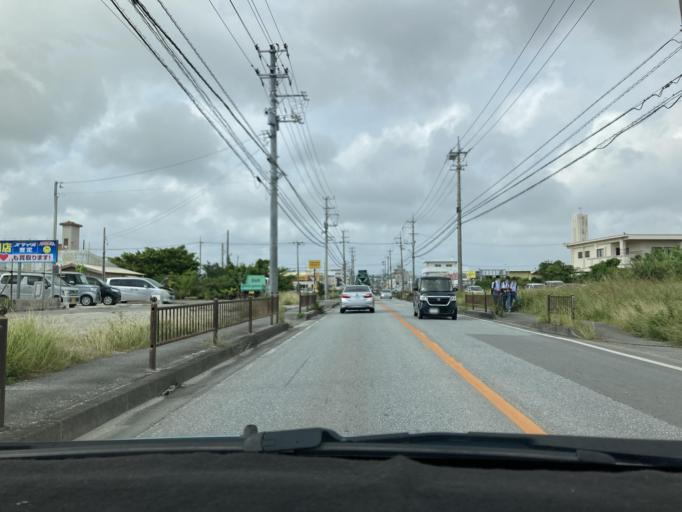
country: JP
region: Okinawa
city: Tomigusuku
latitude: 26.1662
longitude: 127.6682
